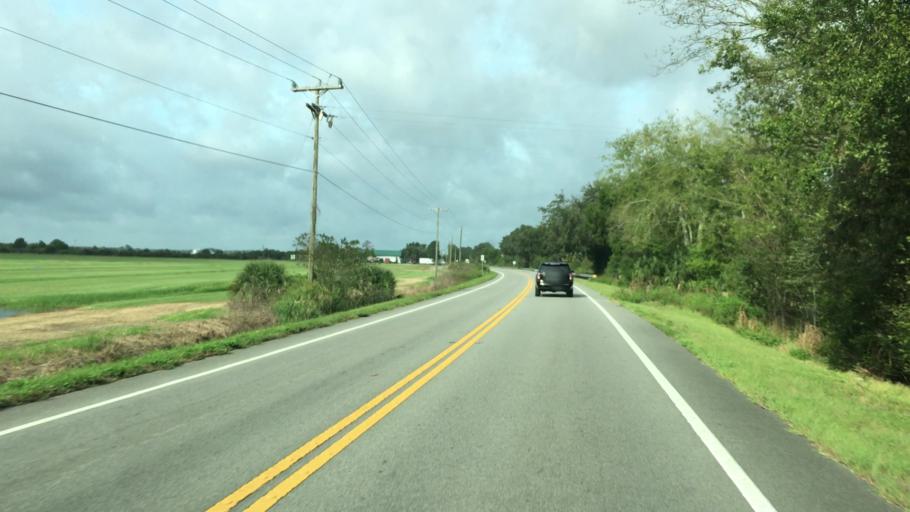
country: US
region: Florida
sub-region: Flagler County
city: Bunnell
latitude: 29.4822
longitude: -81.3493
